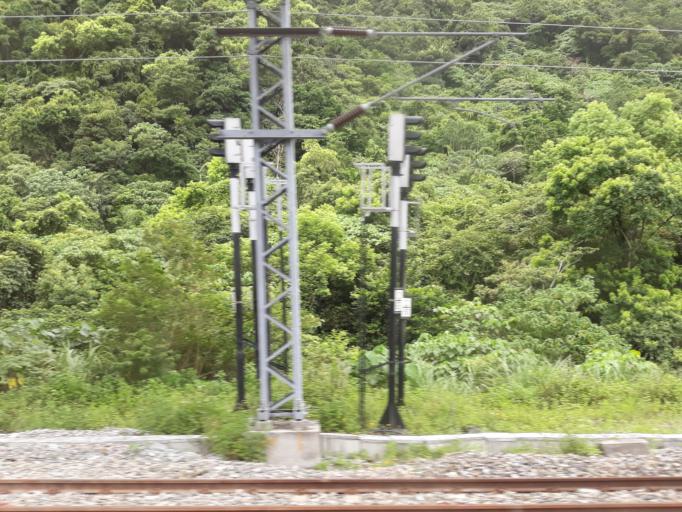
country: TW
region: Taiwan
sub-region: Yilan
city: Yilan
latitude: 24.4480
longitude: 121.7759
